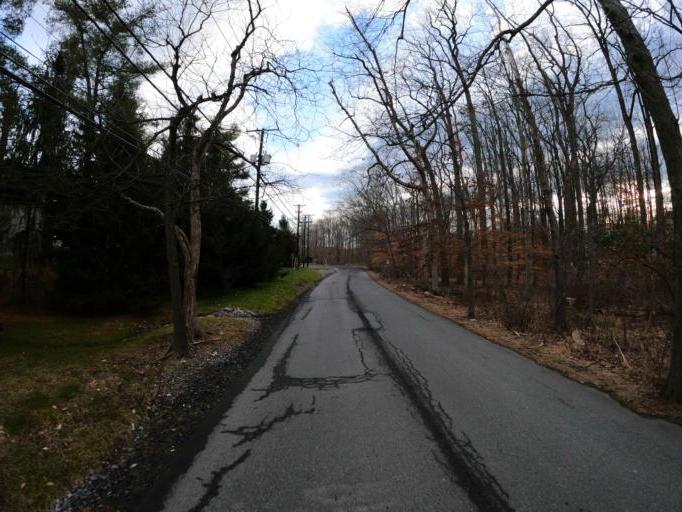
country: US
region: Maryland
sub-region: Montgomery County
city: Olney
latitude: 39.1525
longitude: -77.0551
